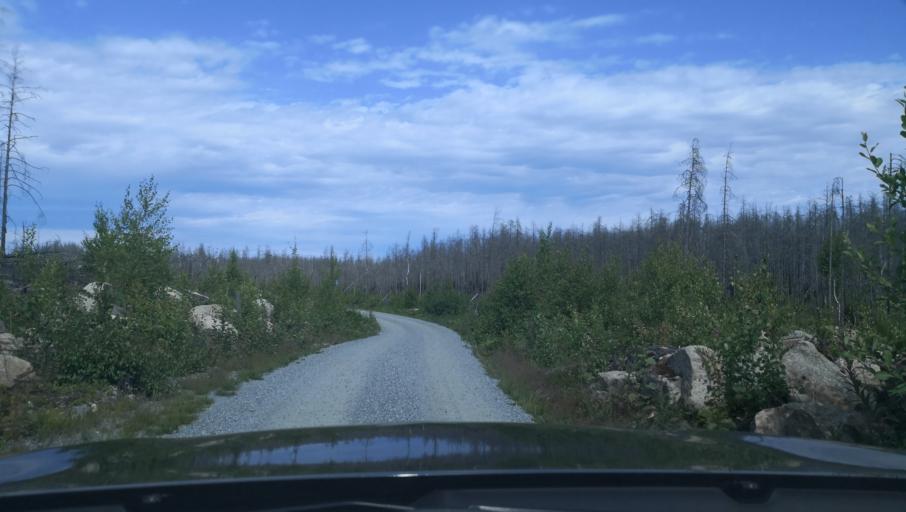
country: SE
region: Vaestmanland
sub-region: Surahammars Kommun
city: Ramnas
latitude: 59.9214
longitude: 16.1660
